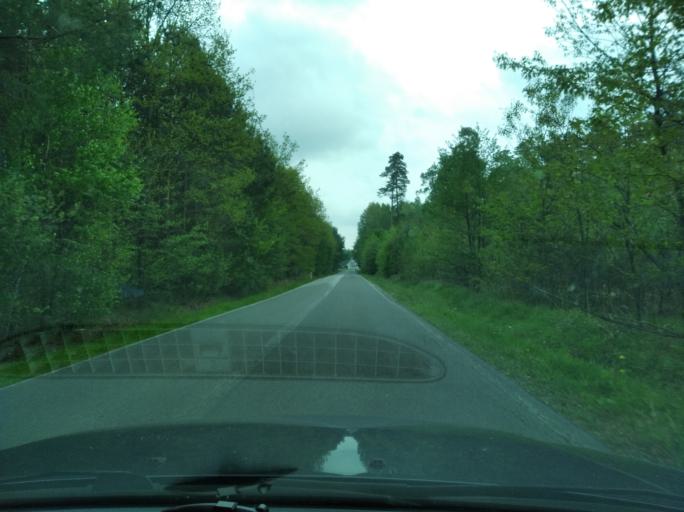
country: PL
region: Subcarpathian Voivodeship
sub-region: Powiat kolbuszowski
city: Kolbuszowa
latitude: 50.1743
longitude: 21.7593
